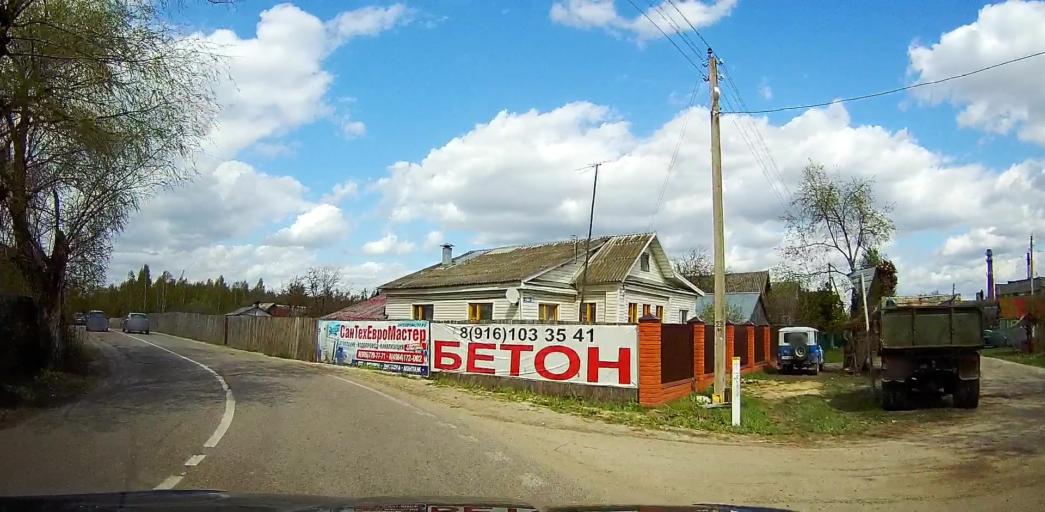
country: RU
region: Moskovskaya
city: Davydovo
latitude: 55.6055
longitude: 38.8480
